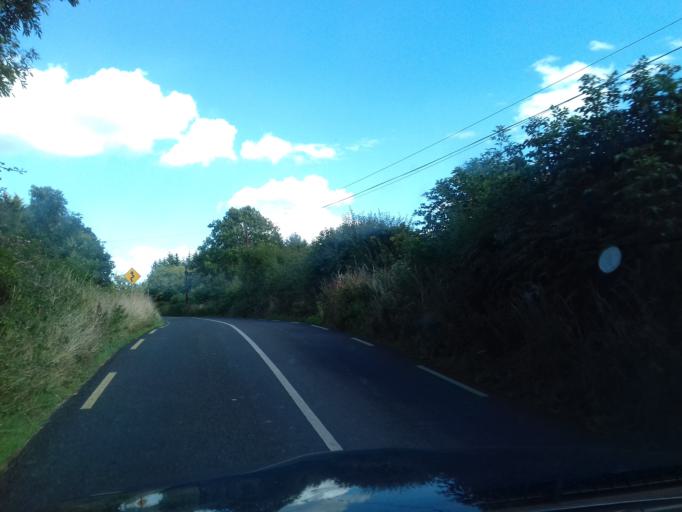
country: IE
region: Leinster
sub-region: Kilkenny
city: Thomastown
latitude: 52.5369
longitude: -7.1003
